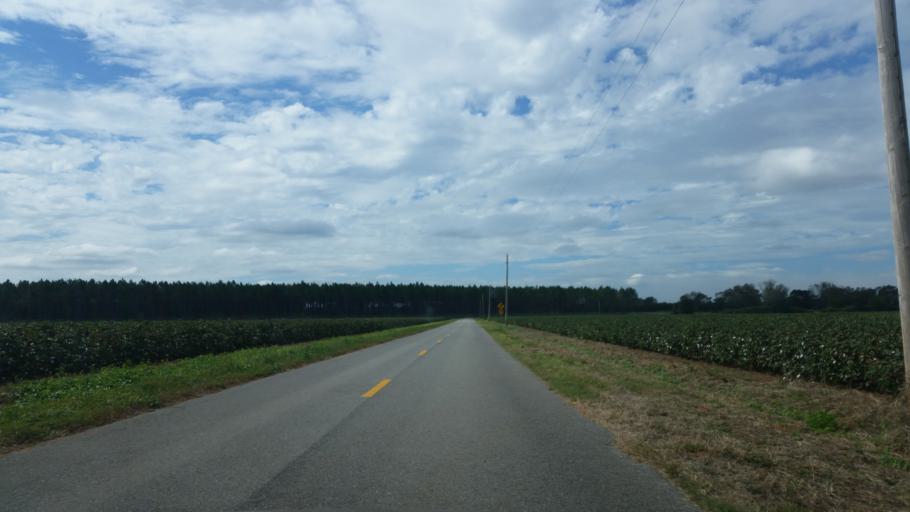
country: US
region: Florida
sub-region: Santa Rosa County
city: Point Baker
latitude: 30.7367
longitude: -87.0270
